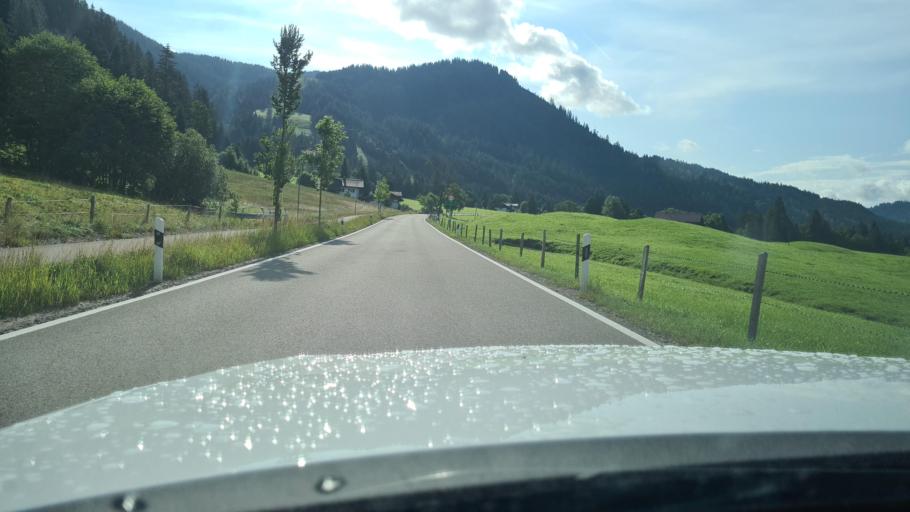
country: DE
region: Bavaria
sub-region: Swabia
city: Balderschwang
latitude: 47.4616
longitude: 10.1219
